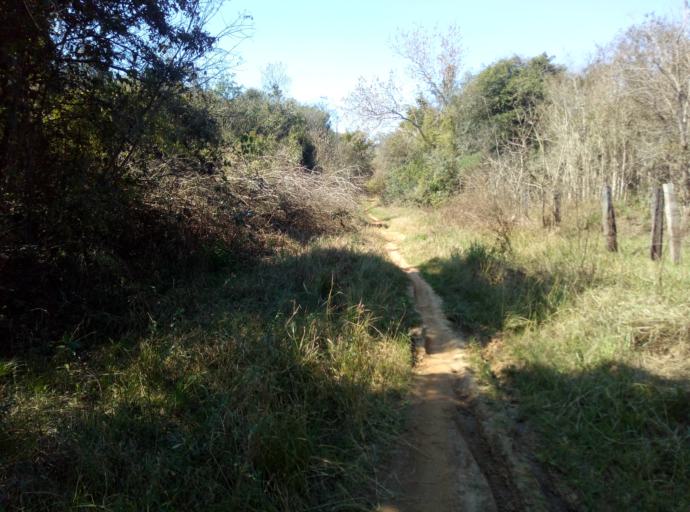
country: PY
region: Caaguazu
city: Doctor Cecilio Baez
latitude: -25.1793
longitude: -56.2227
